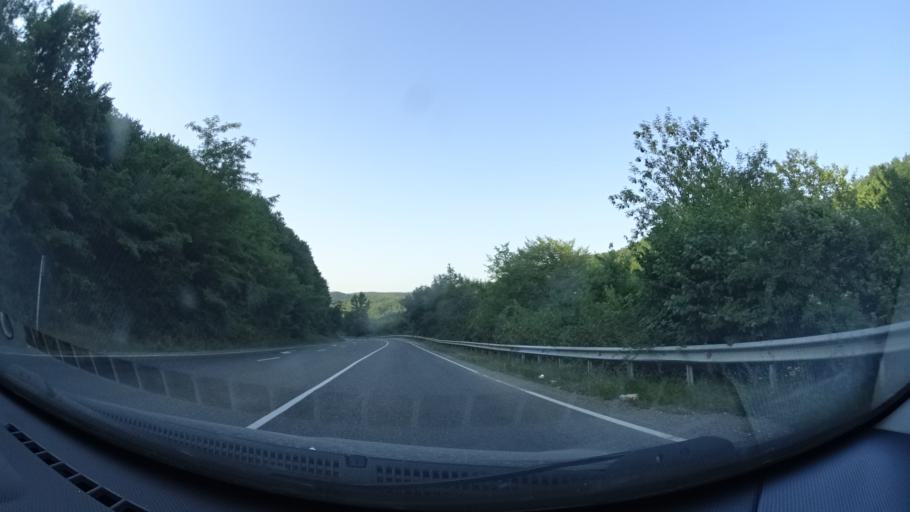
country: GE
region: Kakheti
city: Sighnaghi
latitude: 41.6500
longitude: 45.8328
